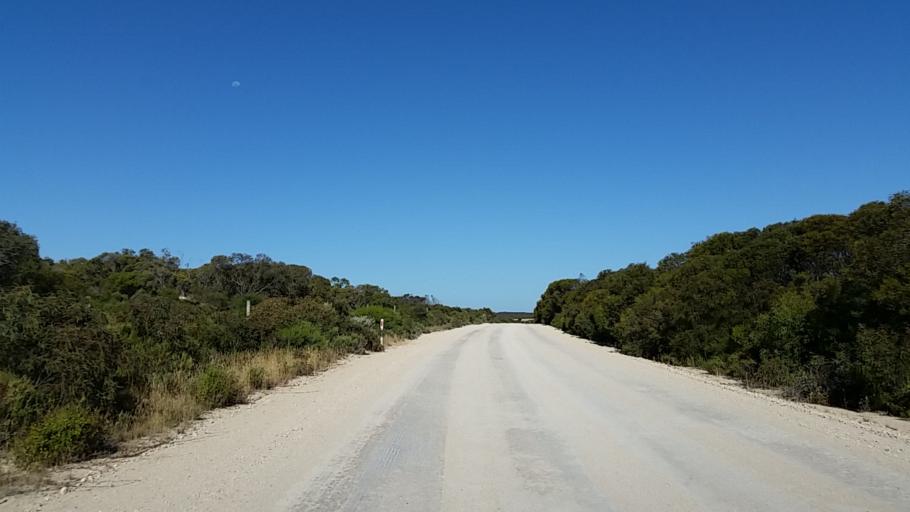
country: AU
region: South Australia
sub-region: Yorke Peninsula
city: Honiton
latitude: -35.2192
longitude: 137.0900
